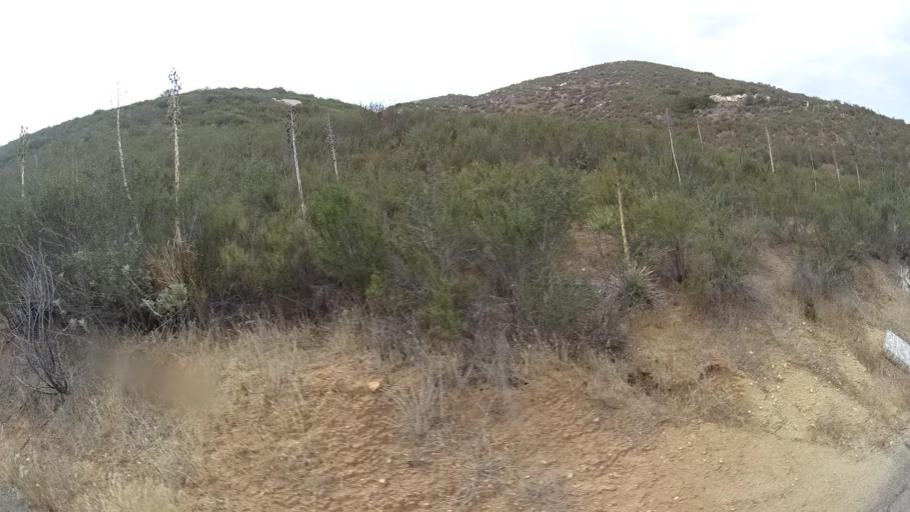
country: US
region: California
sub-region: San Diego County
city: Ramona
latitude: 33.1004
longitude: -116.8581
